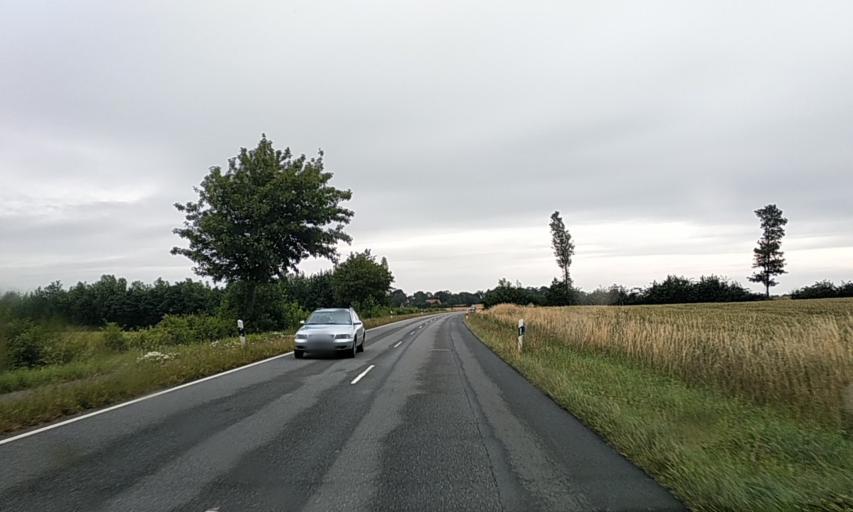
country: DE
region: Schleswig-Holstein
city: Struxdorf
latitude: 54.6251
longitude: 9.6299
